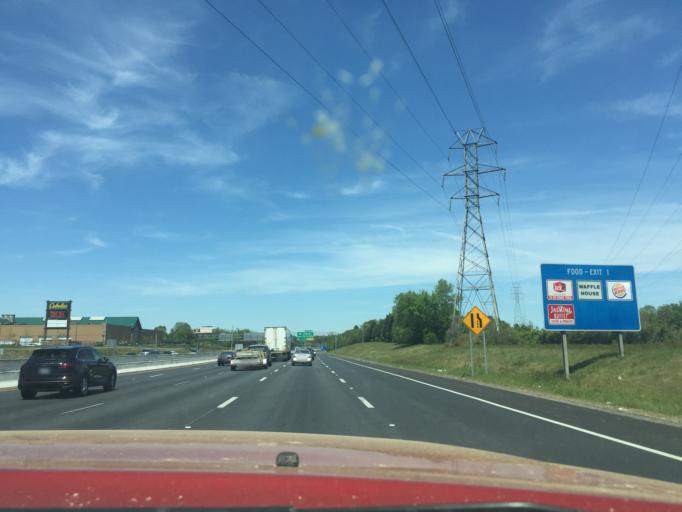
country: US
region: North Carolina
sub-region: Mecklenburg County
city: Pineville
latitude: 35.0963
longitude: -80.9322
